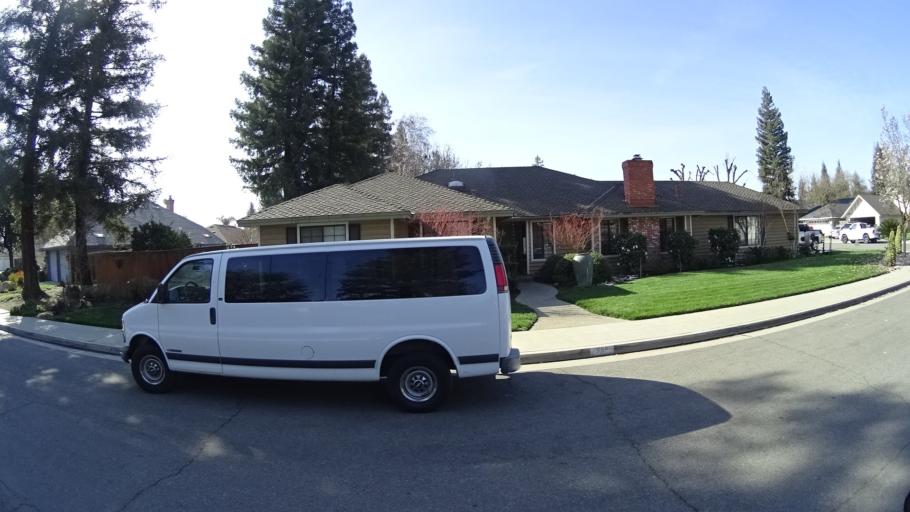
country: US
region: California
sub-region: Fresno County
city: Clovis
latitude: 36.8816
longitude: -119.7747
